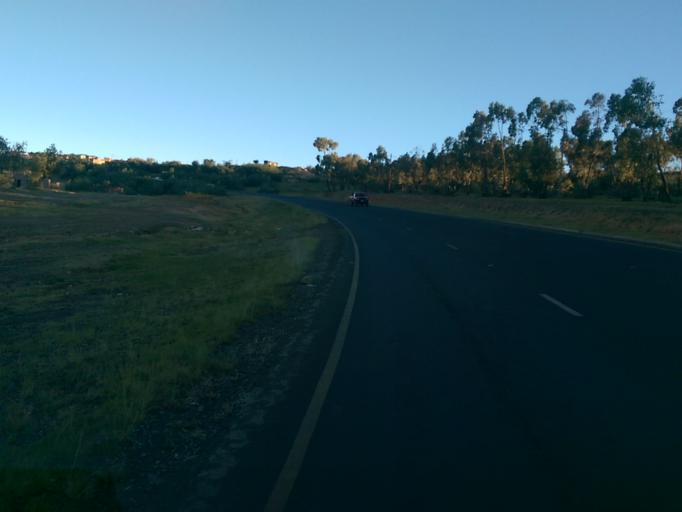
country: LS
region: Maseru
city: Maseru
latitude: -29.4056
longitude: 27.5743
